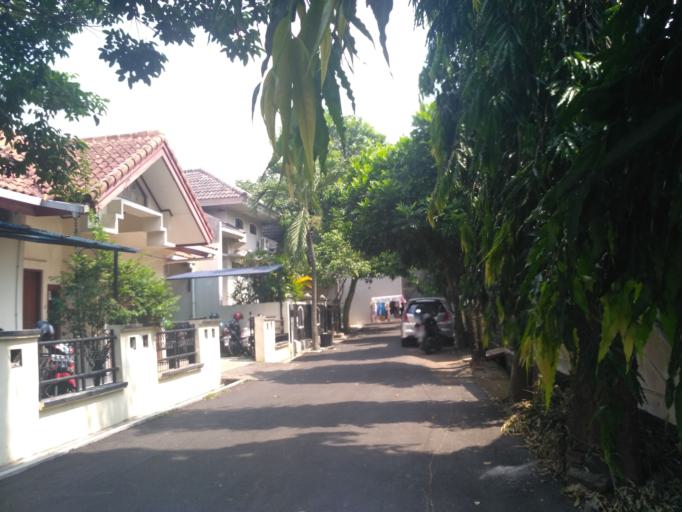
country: ID
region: Central Java
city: Semarang
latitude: -7.0505
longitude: 110.4262
